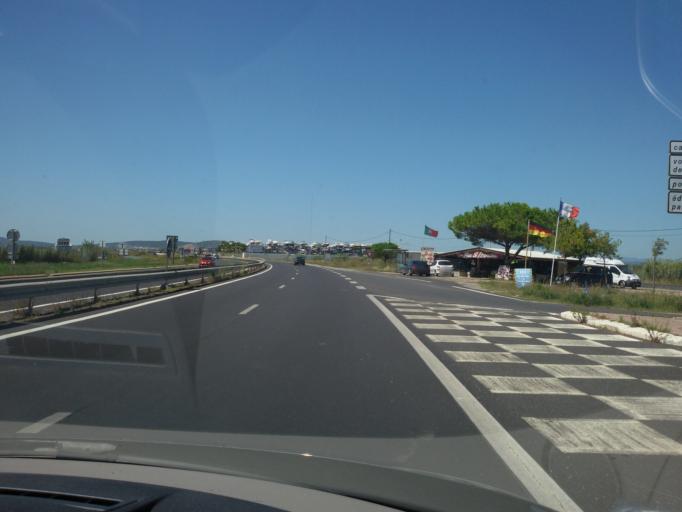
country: FR
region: Languedoc-Roussillon
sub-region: Departement de l'Herault
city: Palavas-les-Flots
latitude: 43.5348
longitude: 3.9142
